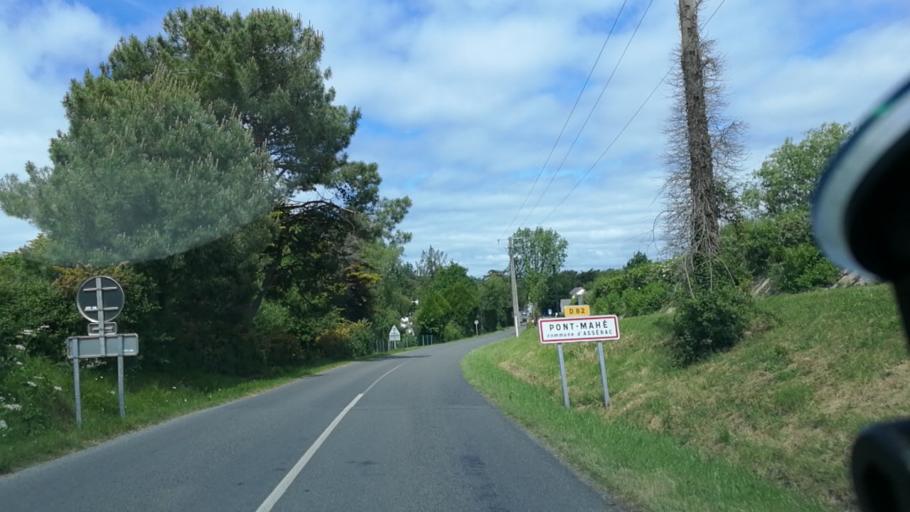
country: FR
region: Brittany
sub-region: Departement du Morbihan
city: Penestin
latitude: 47.4454
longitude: -2.4471
